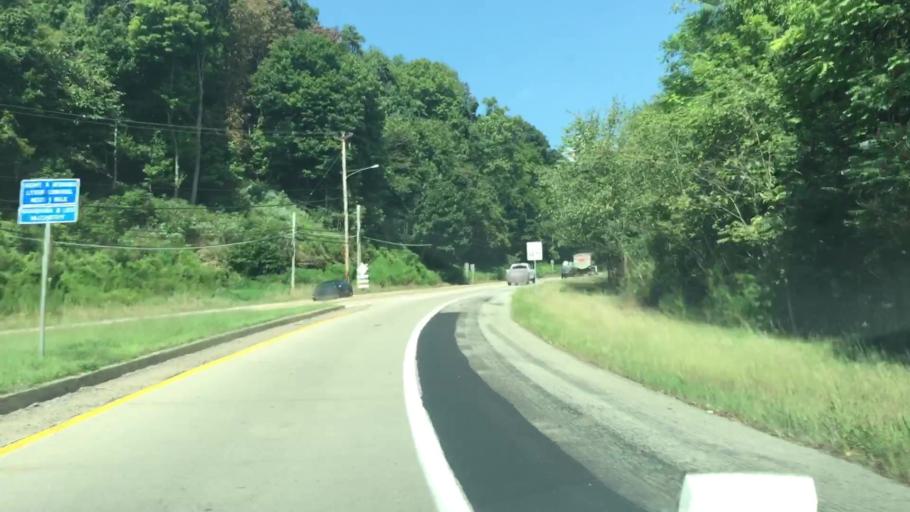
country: US
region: Pennsylvania
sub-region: Allegheny County
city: Edgeworth
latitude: 40.5386
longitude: -80.2003
